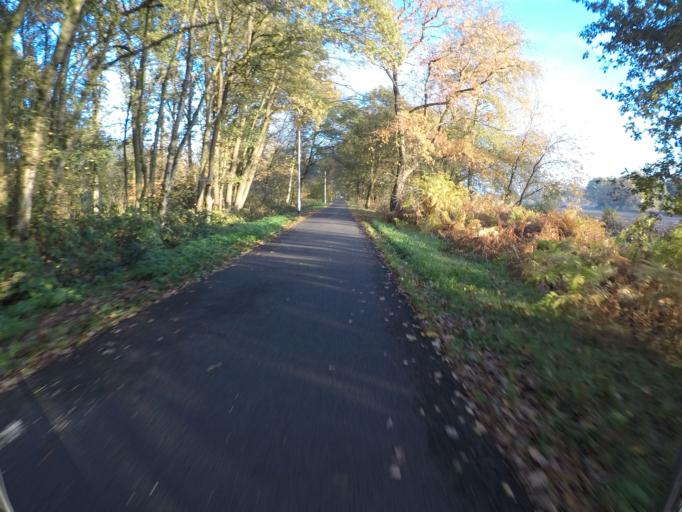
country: BE
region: Flanders
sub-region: Provincie Antwerpen
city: Hulshout
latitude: 51.1054
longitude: 4.8254
